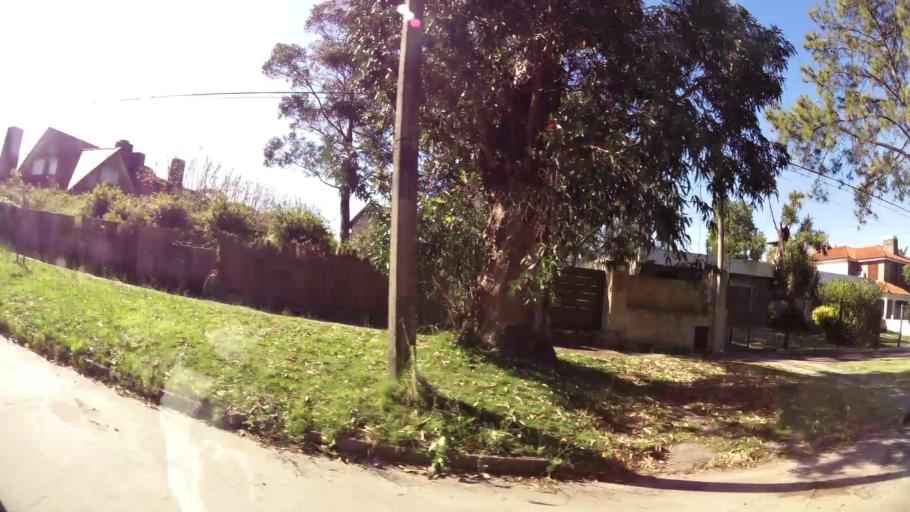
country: UY
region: Canelones
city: Paso de Carrasco
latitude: -34.8821
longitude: -56.0723
